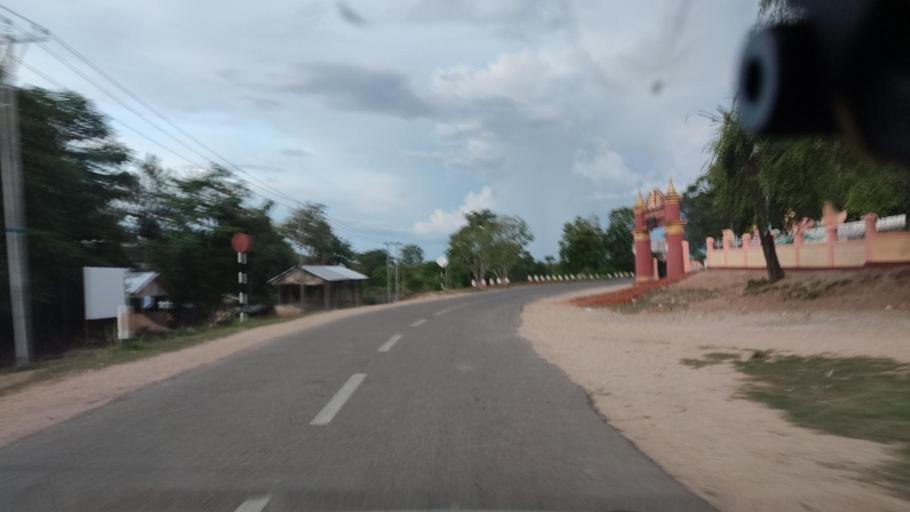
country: MM
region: Magway
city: Minbu
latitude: 20.2262
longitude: 94.8192
